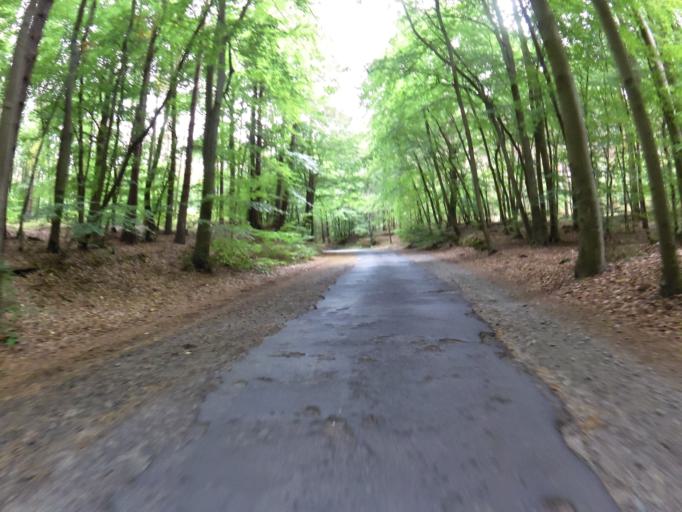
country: DE
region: Mecklenburg-Vorpommern
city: Seebad Heringsdorf
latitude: 53.9497
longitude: 14.1590
